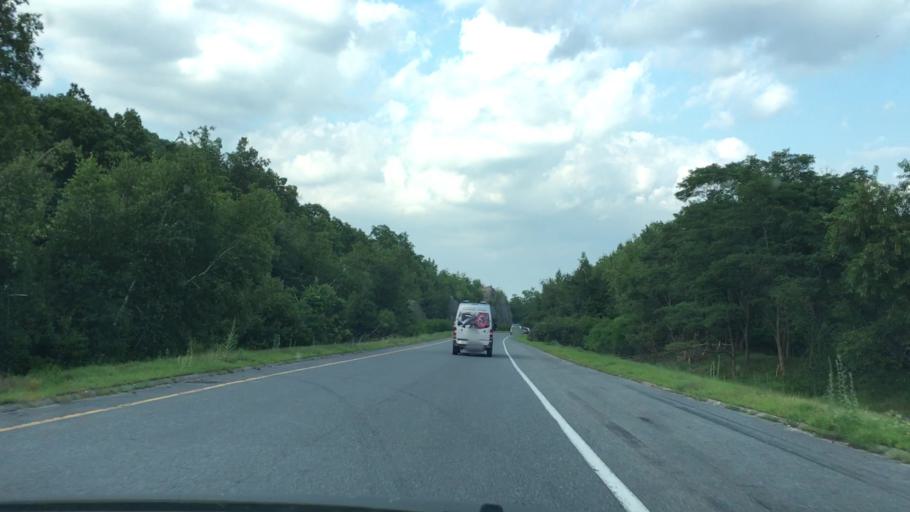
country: US
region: Massachusetts
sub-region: Essex County
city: South Peabody
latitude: 42.5244
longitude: -70.9718
